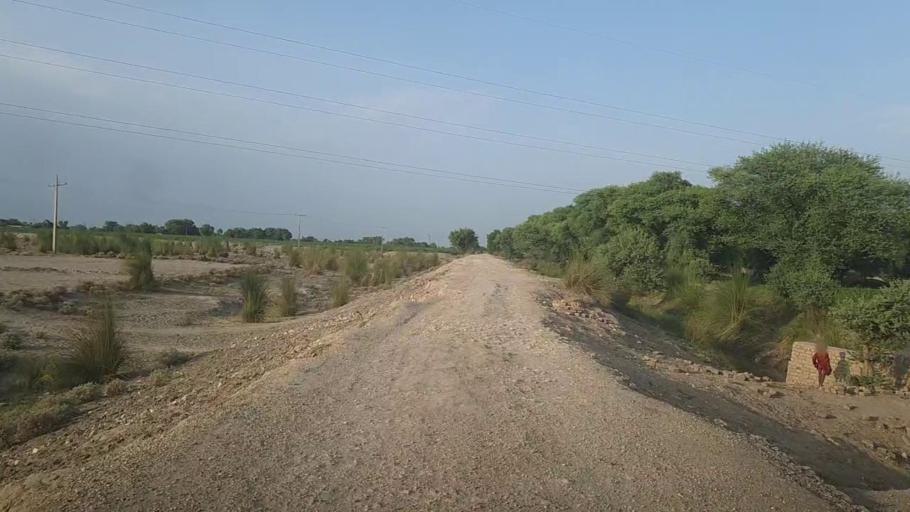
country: PK
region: Sindh
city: Ubauro
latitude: 28.3665
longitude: 69.7957
